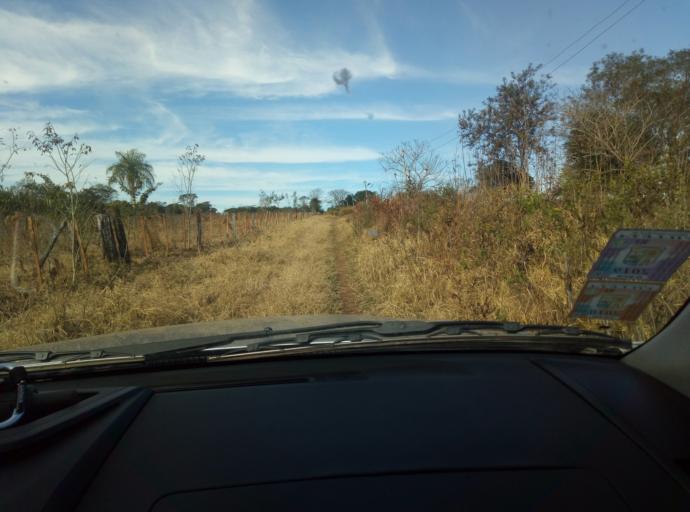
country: PY
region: Caaguazu
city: Carayao
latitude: -25.1720
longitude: -56.2880
